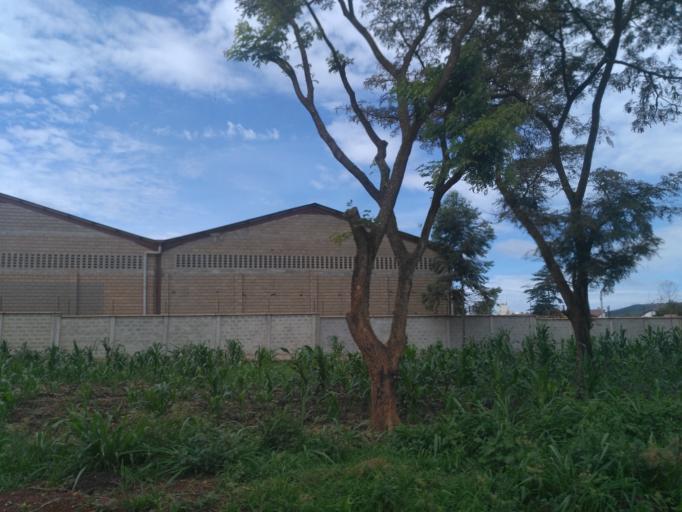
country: UG
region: Eastern Region
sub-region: Jinja District
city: Jinja
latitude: 0.4392
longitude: 33.1838
